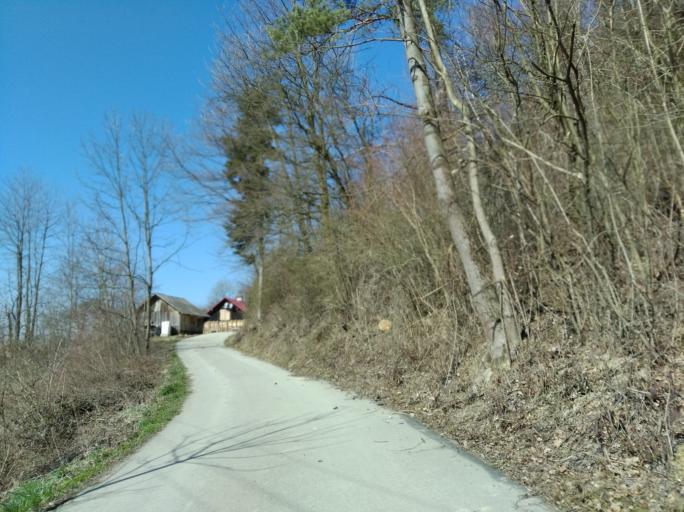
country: PL
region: Subcarpathian Voivodeship
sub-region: Powiat strzyzowski
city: Jawornik
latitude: 49.8611
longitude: 21.8504
